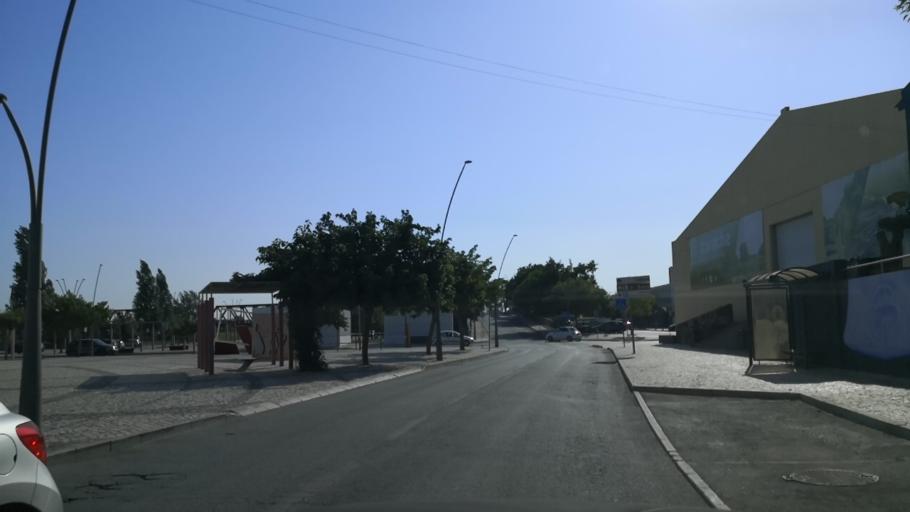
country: PT
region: Santarem
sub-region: Coruche
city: Coruche
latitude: 38.9590
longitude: -8.5215
